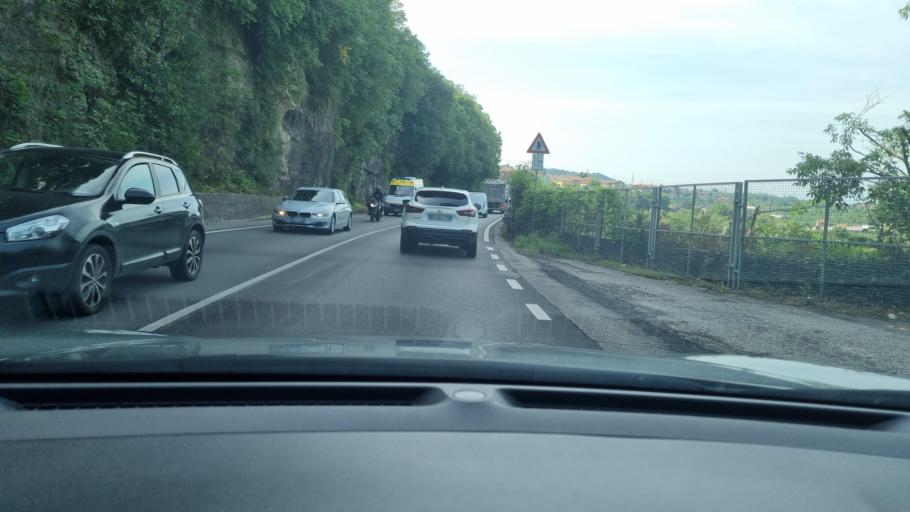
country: IT
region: Lombardy
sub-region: Provincia di Bergamo
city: Villa d'Alme
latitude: 45.7589
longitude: 9.6088
